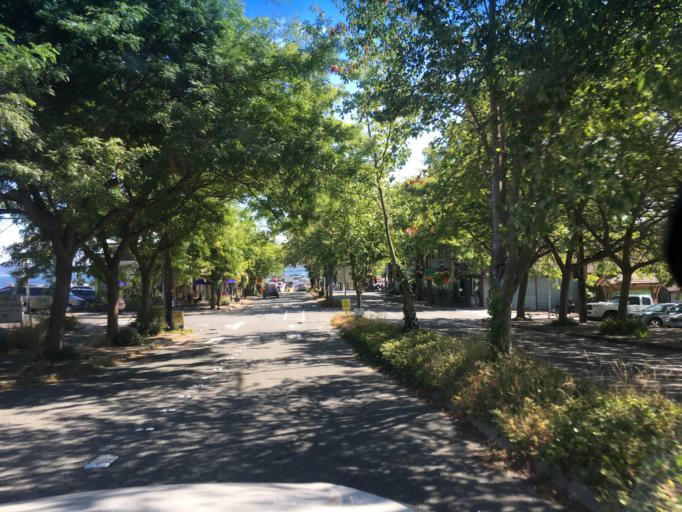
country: US
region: Washington
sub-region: Kitsap County
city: Kingston
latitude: 47.7979
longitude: -122.4976
